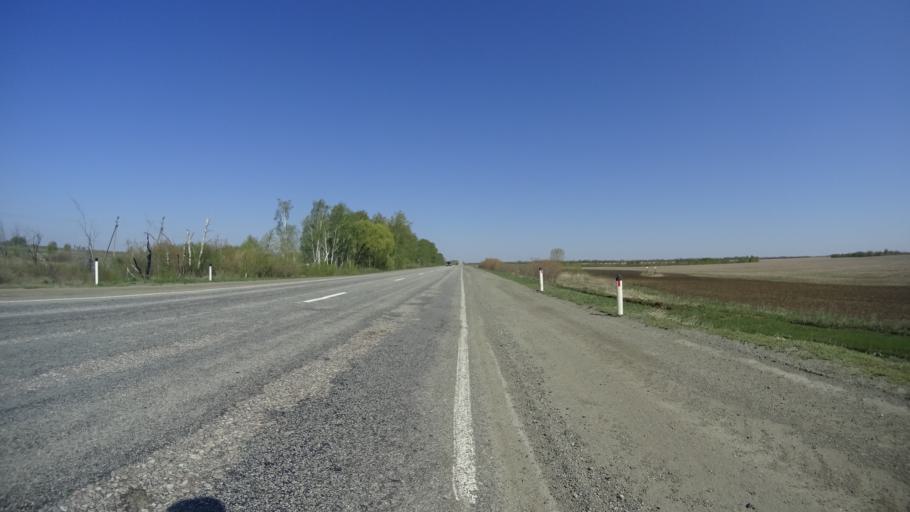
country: RU
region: Chelyabinsk
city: Troitsk
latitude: 54.1965
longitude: 61.4327
